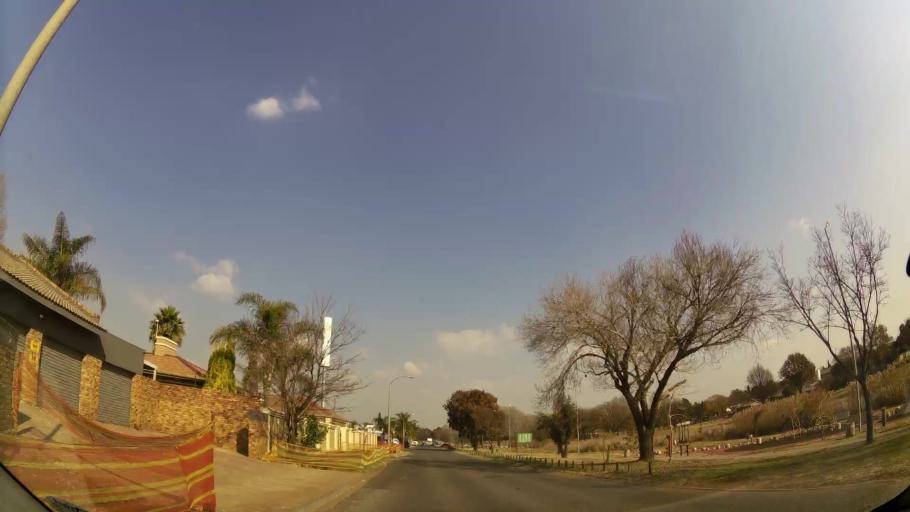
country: ZA
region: Gauteng
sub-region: Ekurhuleni Metropolitan Municipality
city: Benoni
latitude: -26.1526
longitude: 28.2890
